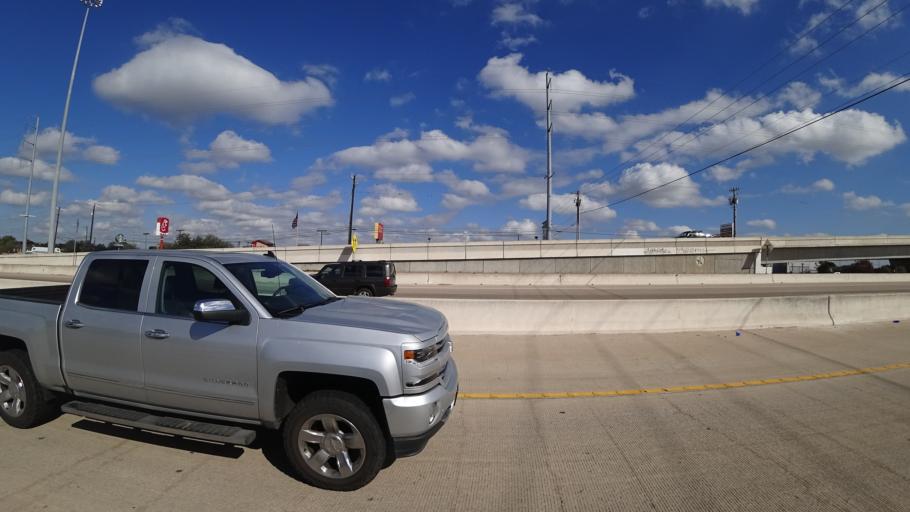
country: US
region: Texas
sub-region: Travis County
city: Austin
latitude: 30.2192
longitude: -97.7570
